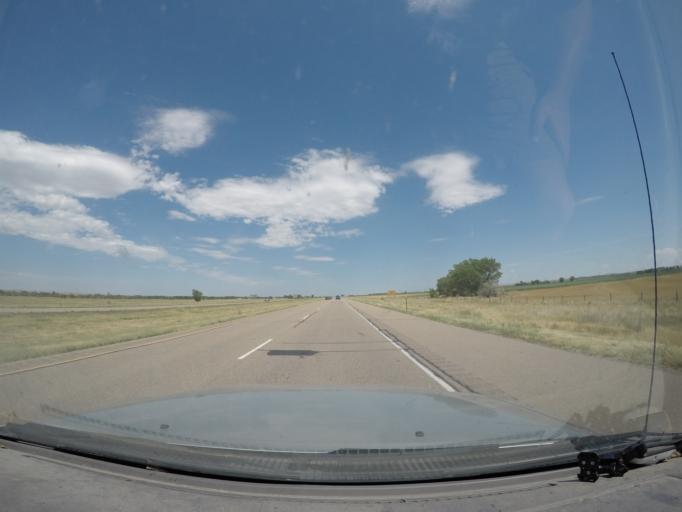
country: US
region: Colorado
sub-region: Sedgwick County
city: Julesburg
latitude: 41.0383
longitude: -102.1213
